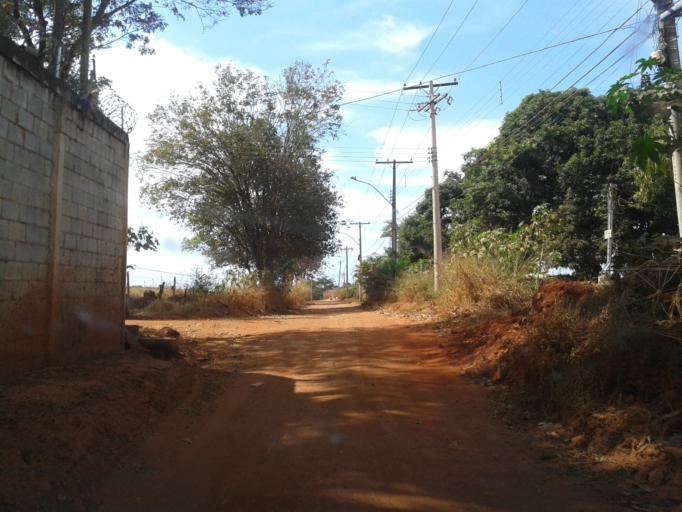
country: BR
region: Goias
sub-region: Goiania
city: Goiania
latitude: -16.6414
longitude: -49.3440
